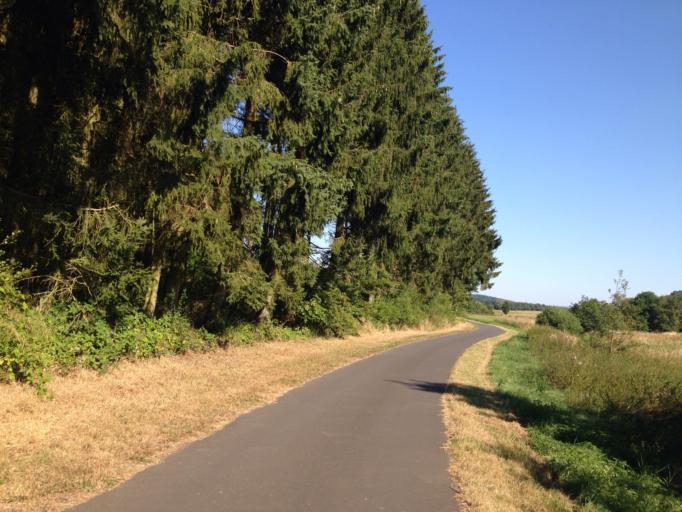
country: DE
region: Hesse
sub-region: Regierungsbezirk Giessen
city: Rabenau
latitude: 50.6415
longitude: 8.9128
